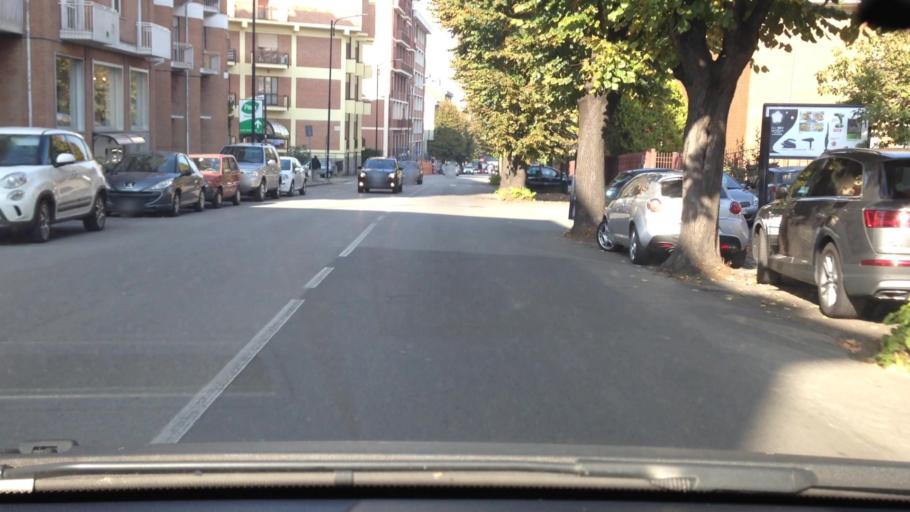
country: IT
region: Piedmont
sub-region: Provincia di Asti
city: Asti
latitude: 44.9052
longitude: 8.1962
